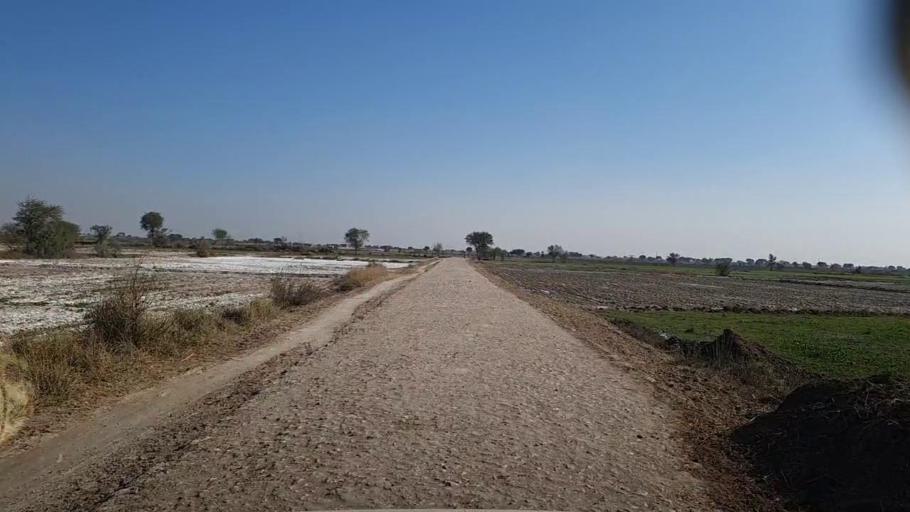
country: PK
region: Sindh
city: Khairpur
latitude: 27.9279
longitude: 69.7323
